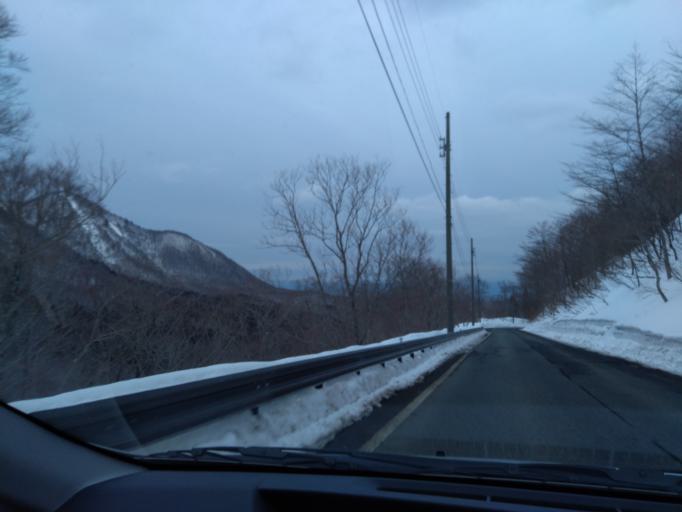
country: JP
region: Iwate
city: Kitakami
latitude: 39.2377
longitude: 140.9112
